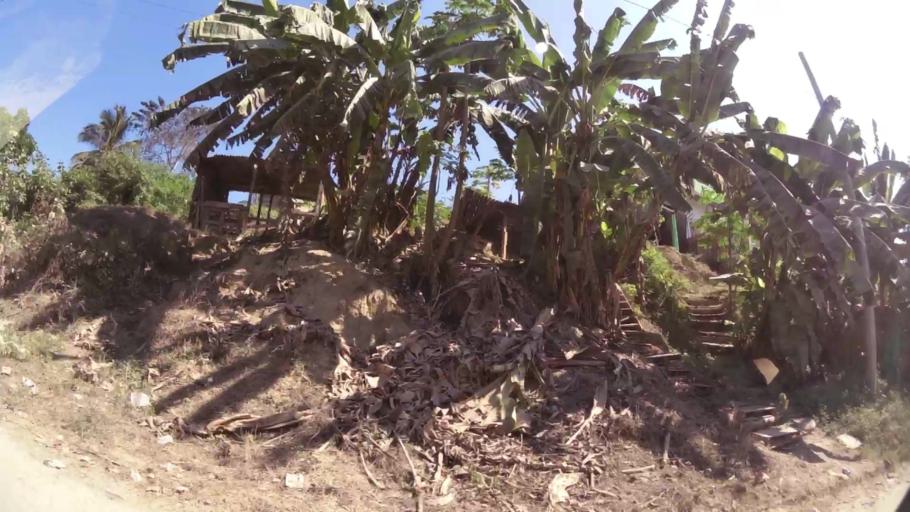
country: CO
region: Bolivar
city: Cartagena
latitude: 10.3709
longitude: -75.4948
